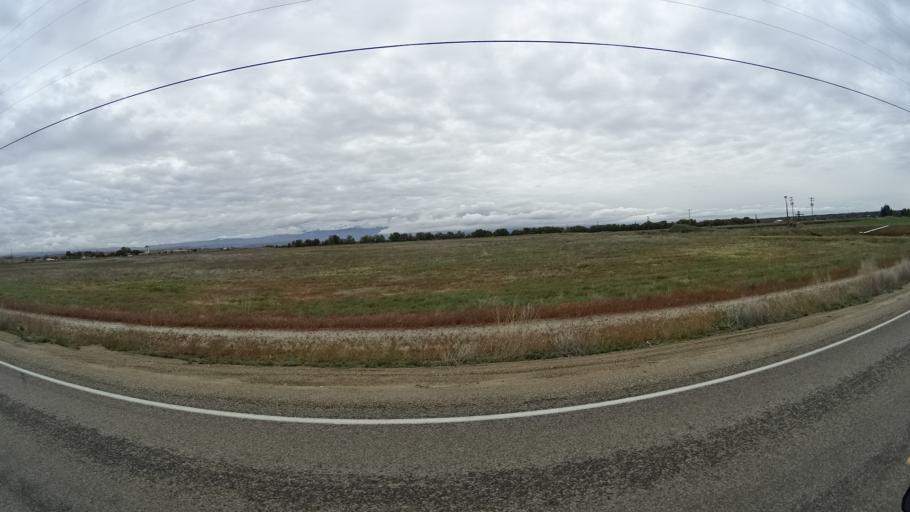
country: US
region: Idaho
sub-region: Ada County
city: Star
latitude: 43.7148
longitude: -116.4435
